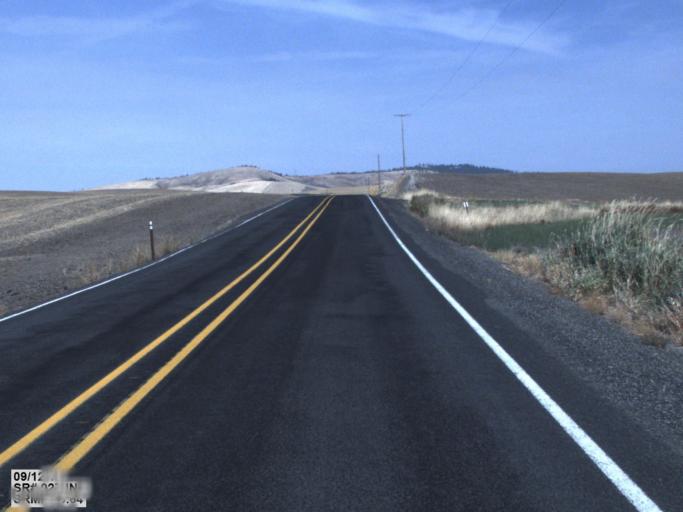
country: US
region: Idaho
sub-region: Benewah County
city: Plummer
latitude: 47.2691
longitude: -117.1313
